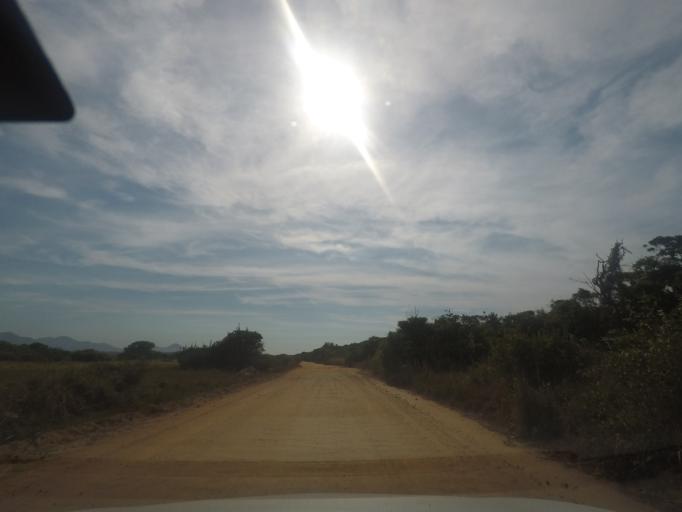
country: BR
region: Rio de Janeiro
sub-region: Marica
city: Marica
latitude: -22.9606
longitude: -42.8603
